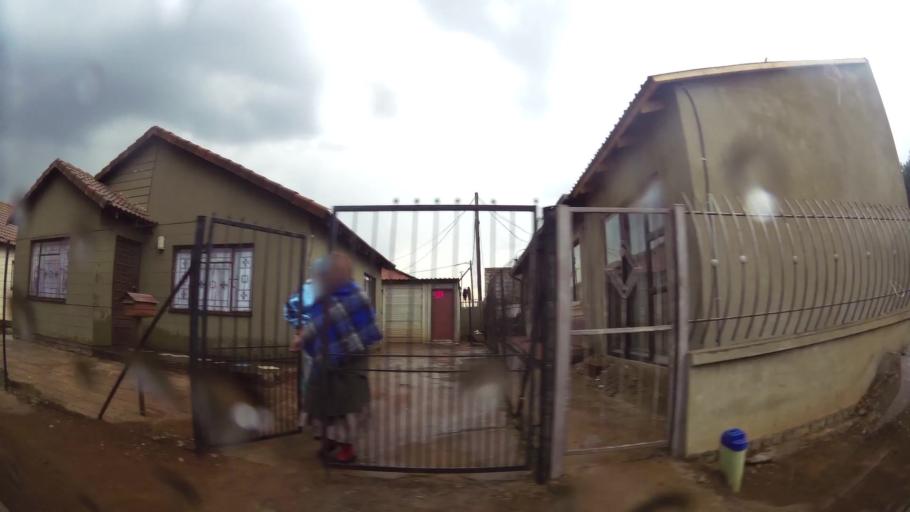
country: ZA
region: Gauteng
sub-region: Ekurhuleni Metropolitan Municipality
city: Germiston
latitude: -26.3619
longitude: 28.1389
